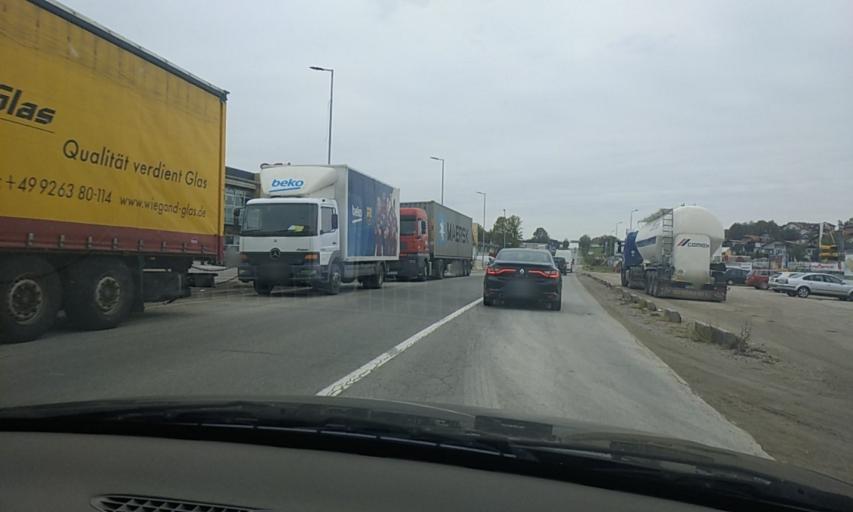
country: BA
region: Republika Srpska
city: Prnjavor
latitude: 44.8563
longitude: 17.6802
